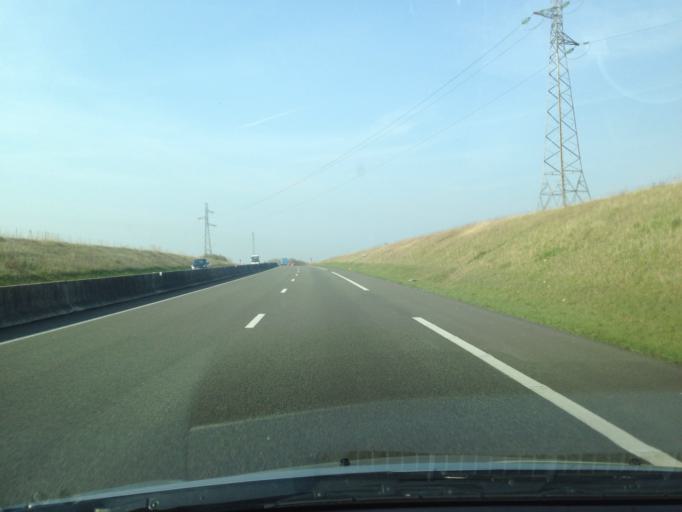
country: FR
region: Picardie
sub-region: Departement de la Somme
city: Sailly-Flibeaucourt
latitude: 50.1960
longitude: 1.7591
